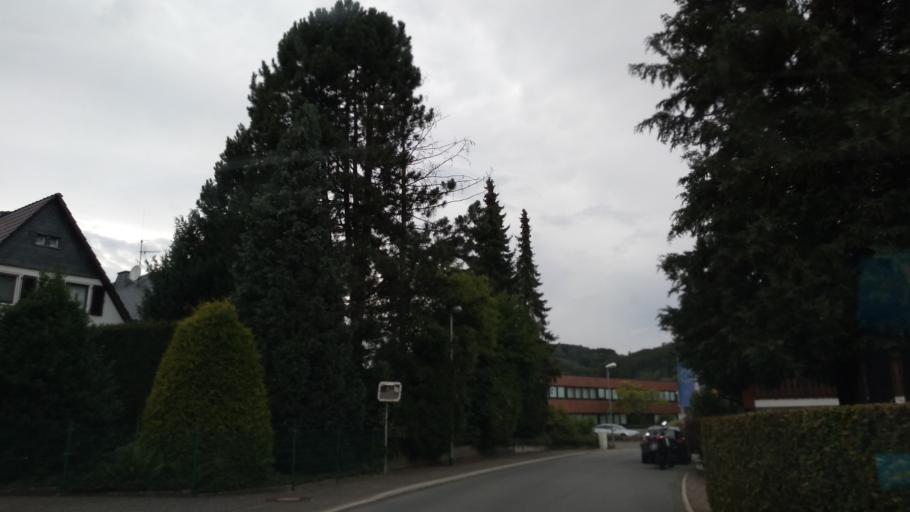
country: DE
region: North Rhine-Westphalia
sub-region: Regierungsbezirk Arnsberg
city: Herscheid
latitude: 51.1895
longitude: 7.8023
